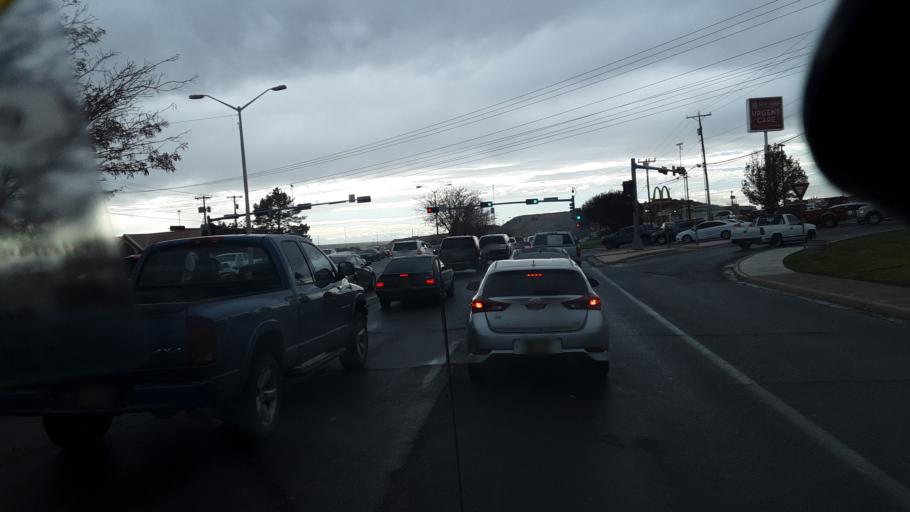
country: US
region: New Mexico
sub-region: San Juan County
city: Flora Vista
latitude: 36.7672
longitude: -108.1480
